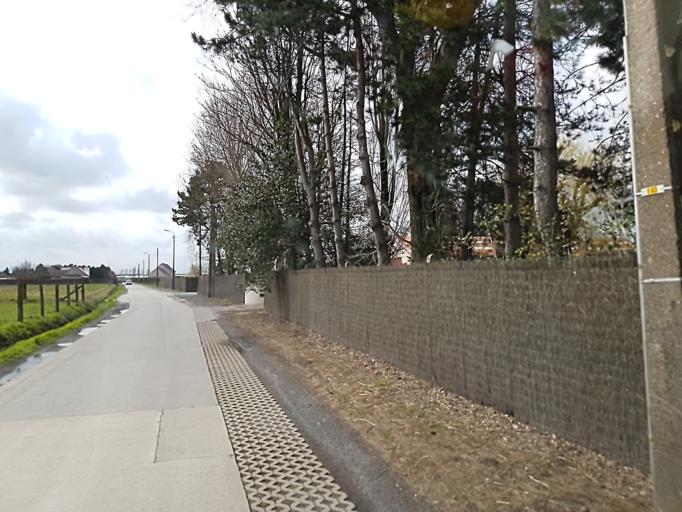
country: BE
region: Flanders
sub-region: Provincie Oost-Vlaanderen
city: Kruishoutem
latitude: 50.9255
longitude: 3.4948
